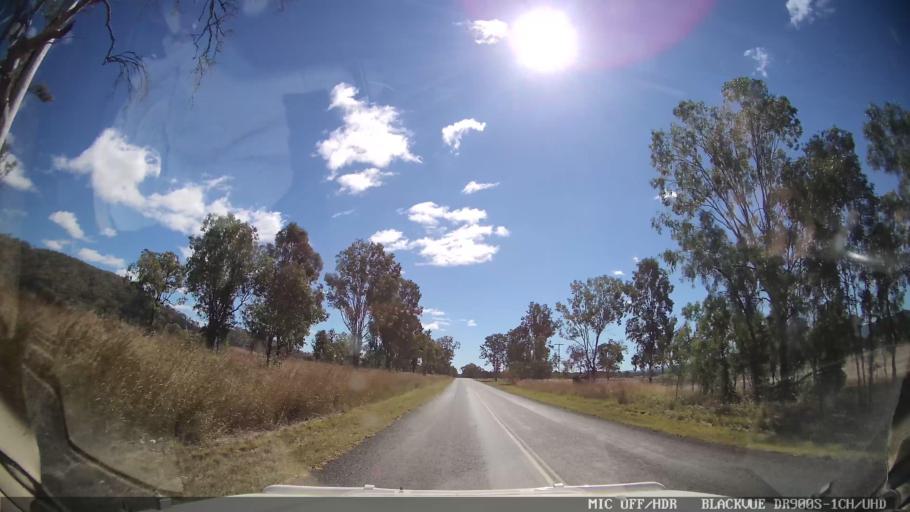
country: AU
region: Queensland
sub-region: Gladstone
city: Toolooa
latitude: -24.4520
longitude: 151.3459
